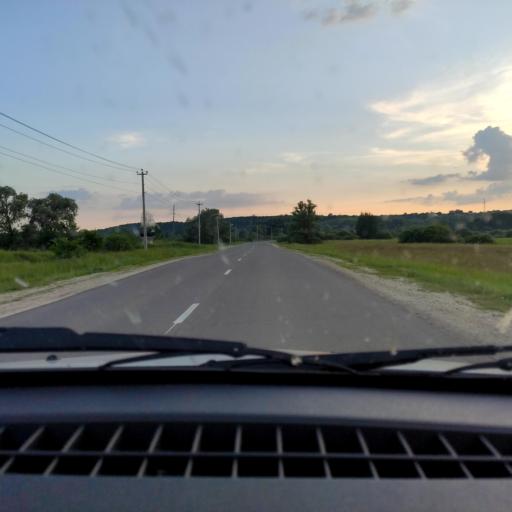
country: RU
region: Voronezj
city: Ramon'
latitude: 51.9513
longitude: 39.3912
